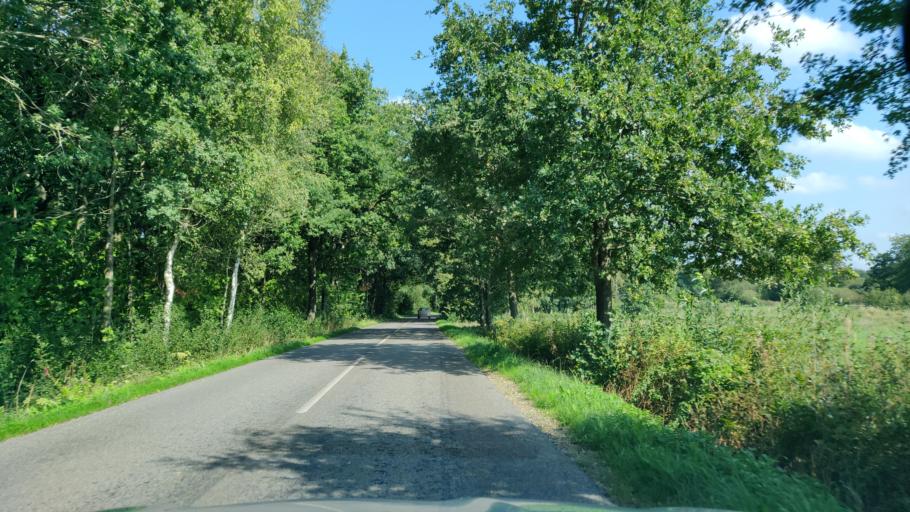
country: DK
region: Central Jutland
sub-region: Herning Kommune
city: Avlum
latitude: 56.2448
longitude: 8.8742
